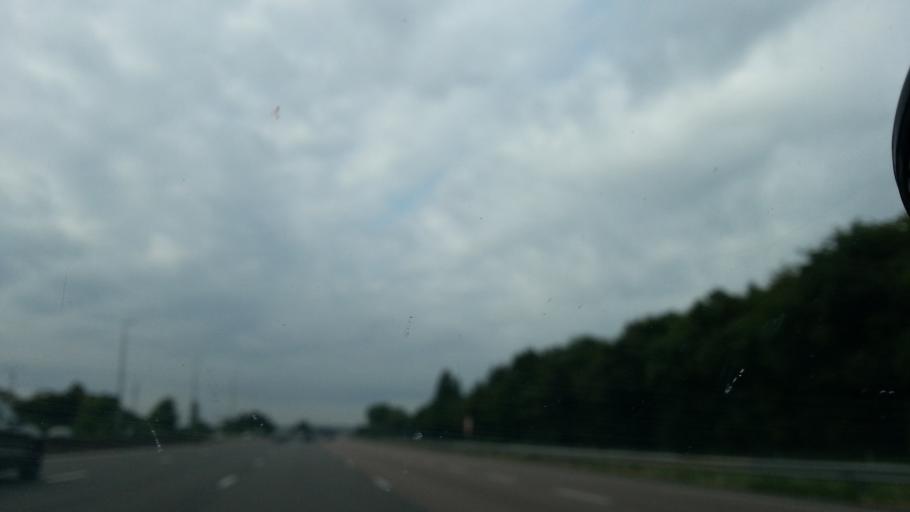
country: FR
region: Bourgogne
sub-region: Departement de la Cote-d'Or
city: Bligny-les-Beaune
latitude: 46.9591
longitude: 4.8355
